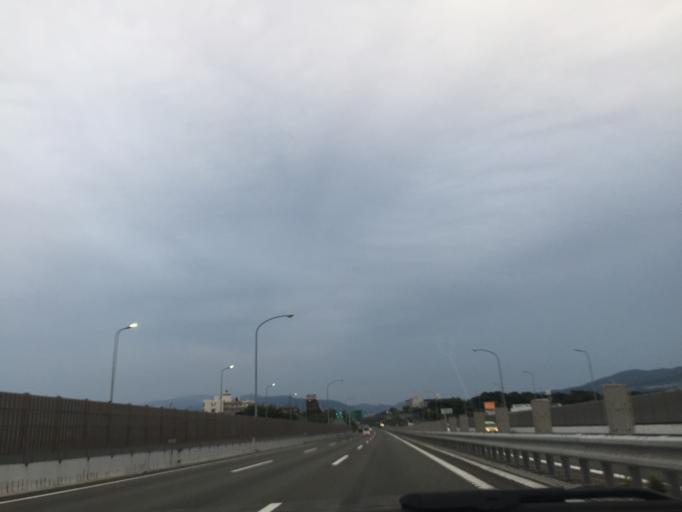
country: JP
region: Hyogo
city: Kawanishi
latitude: 34.8110
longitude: 135.4133
